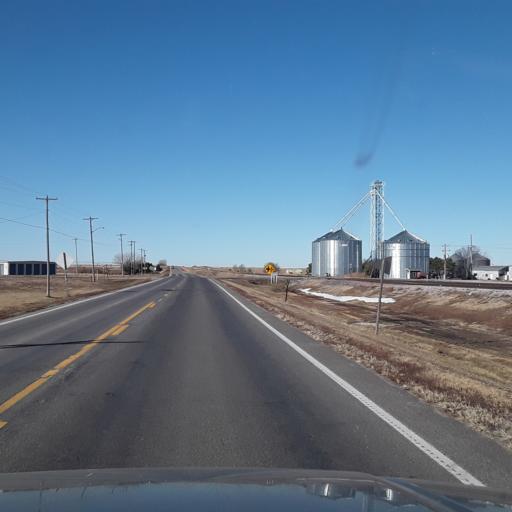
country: US
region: Nebraska
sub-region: Phelps County
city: Holdrege
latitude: 40.4802
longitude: -99.5107
